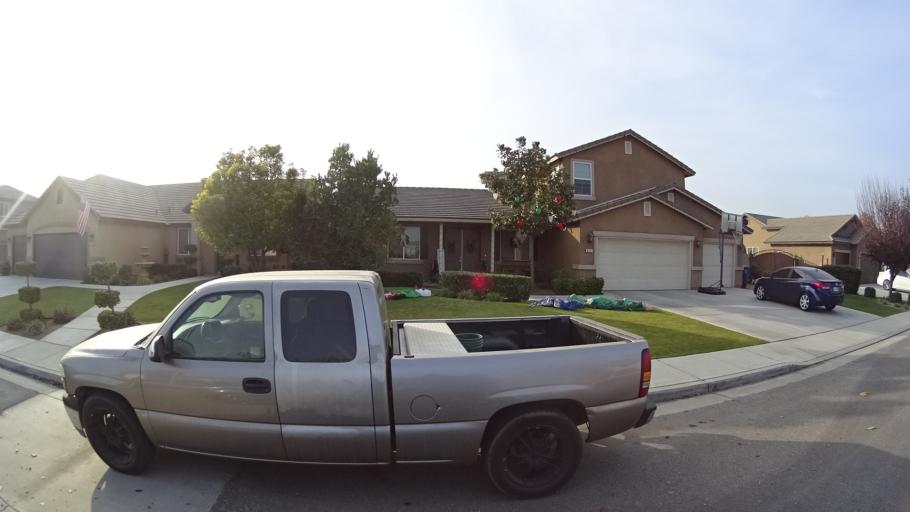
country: US
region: California
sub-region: Kern County
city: Greenacres
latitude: 35.4358
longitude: -119.1115
